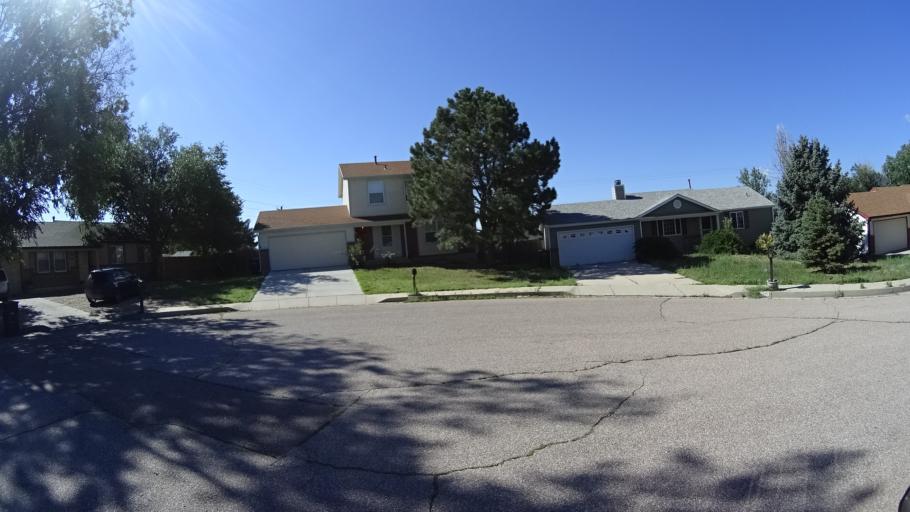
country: US
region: Colorado
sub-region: El Paso County
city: Air Force Academy
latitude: 38.9408
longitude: -104.7850
